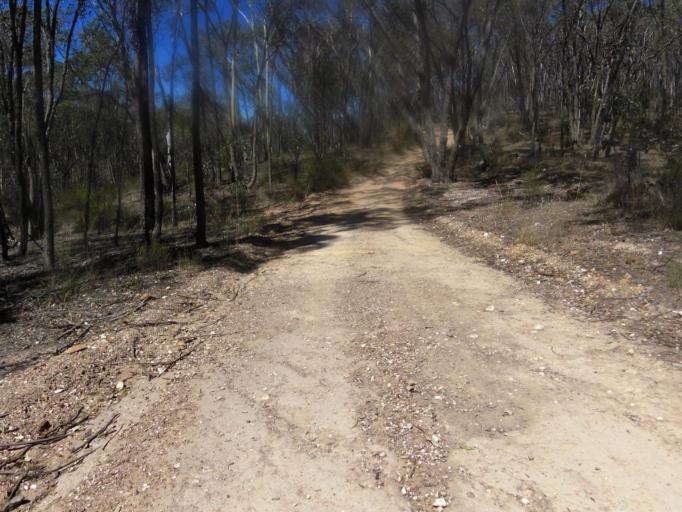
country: AU
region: Victoria
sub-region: Mount Alexander
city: Castlemaine
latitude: -37.0557
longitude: 144.1887
